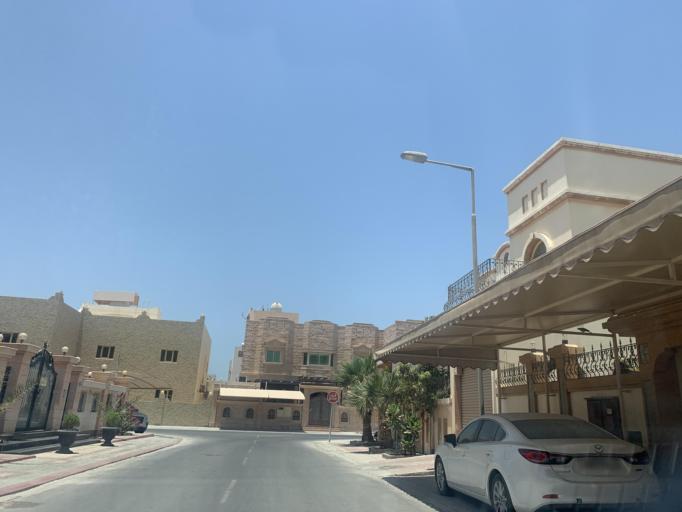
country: BH
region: Muharraq
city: Al Muharraq
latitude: 26.2856
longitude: 50.6198
